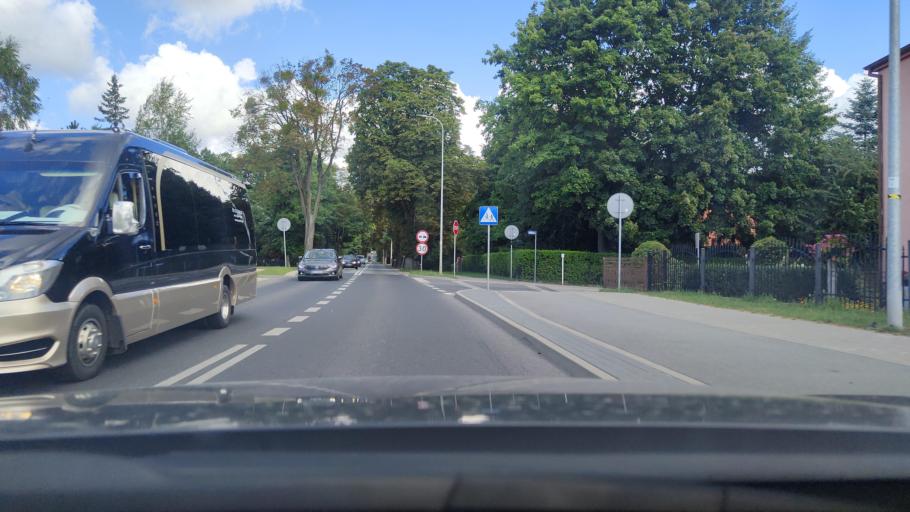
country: PL
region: Pomeranian Voivodeship
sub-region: Powiat wejherowski
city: Wejherowo
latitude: 54.6128
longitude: 18.2268
